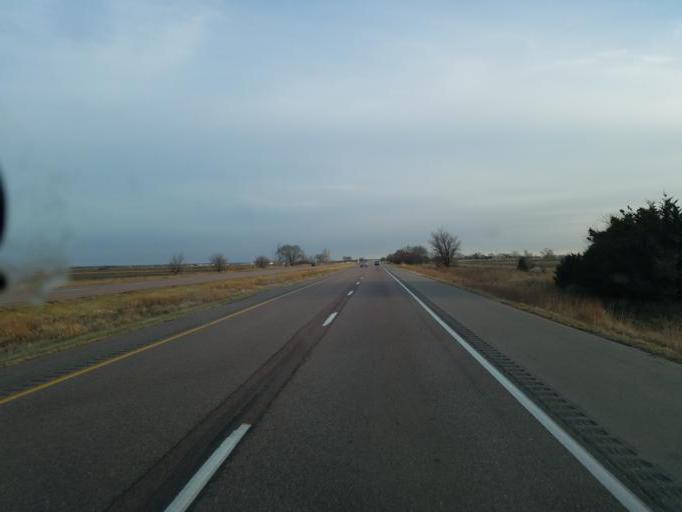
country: US
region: Iowa
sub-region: Monona County
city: Onawa
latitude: 42.0584
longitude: -96.1583
